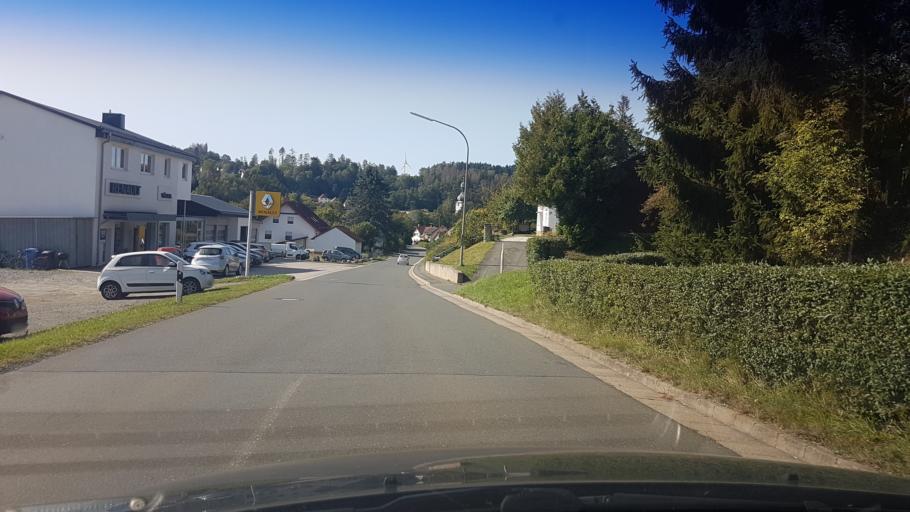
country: DE
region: Bavaria
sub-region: Upper Franconia
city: Marktschorgast
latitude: 50.0944
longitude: 11.6615
